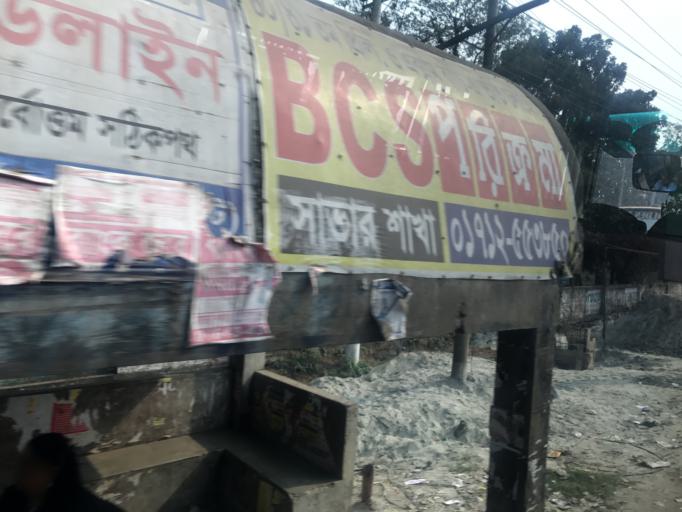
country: BD
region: Dhaka
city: Tungi
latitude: 23.8898
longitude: 90.2722
